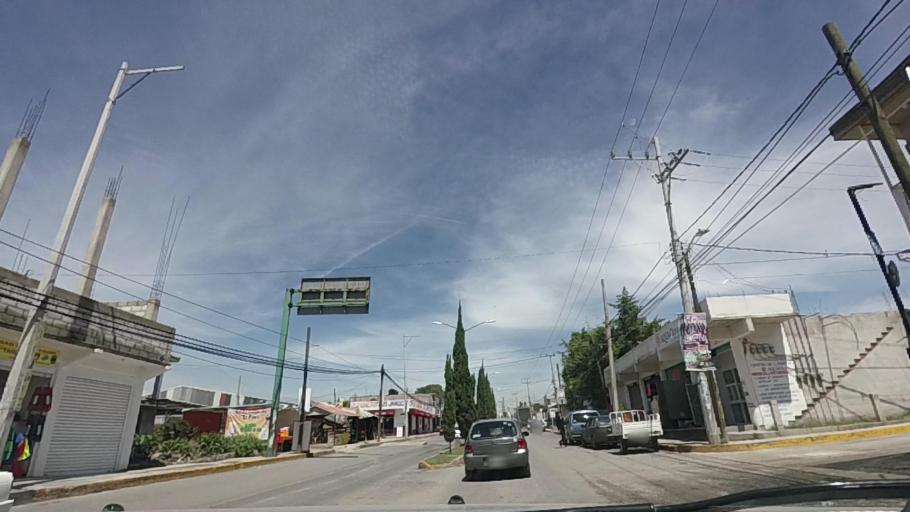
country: MX
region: Mexico
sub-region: Huehuetoca
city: Casa Nueva
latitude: 19.8308
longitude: -99.2218
